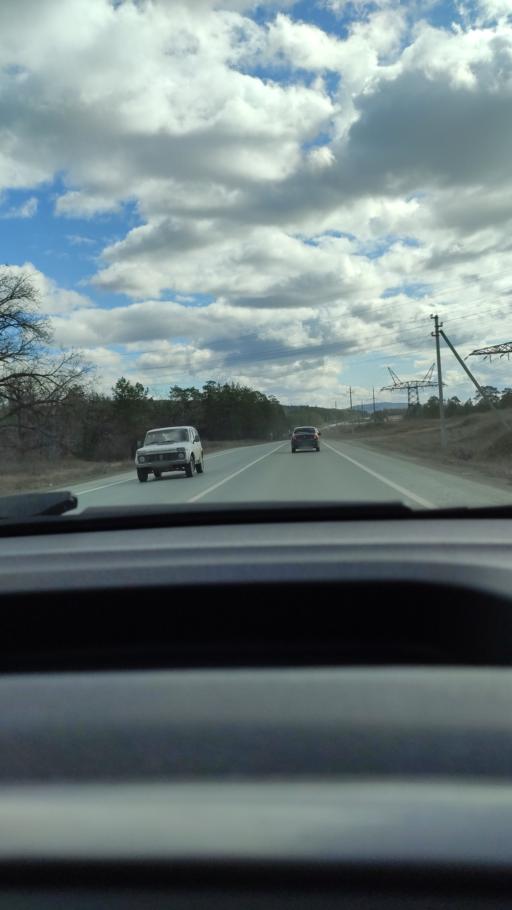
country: RU
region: Samara
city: Kurumoch
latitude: 53.4773
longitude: 50.0562
